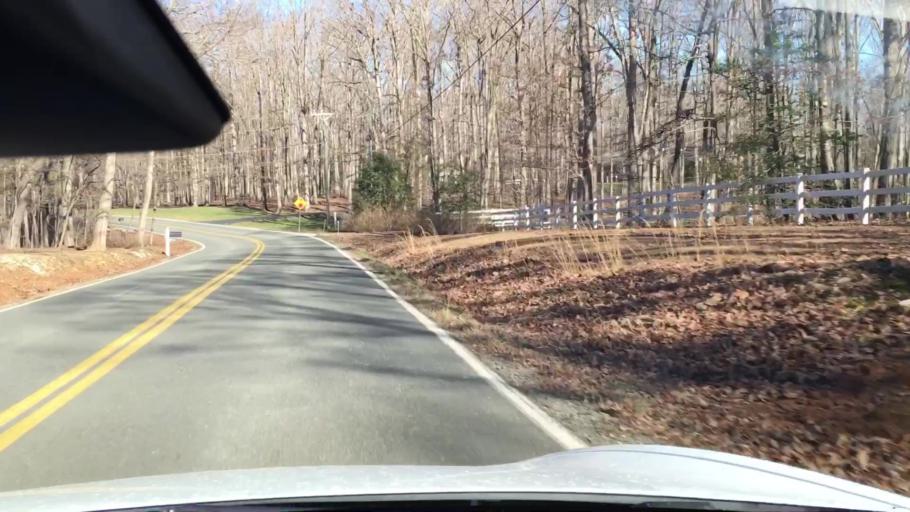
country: US
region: Virginia
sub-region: Powhatan County
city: Powhatan
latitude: 37.5581
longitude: -77.7989
